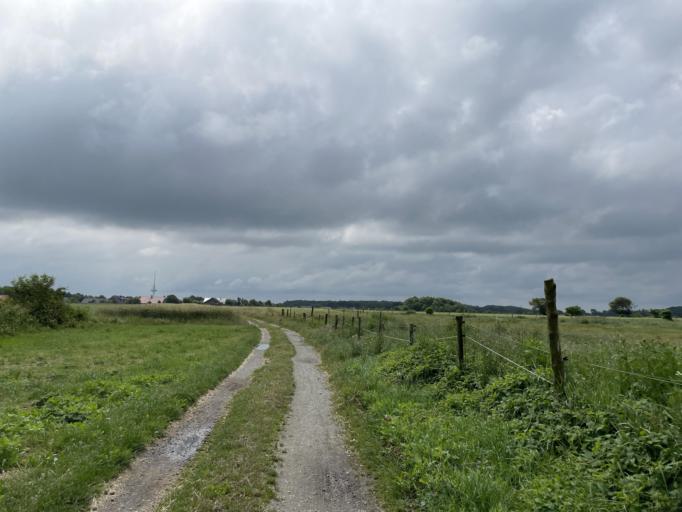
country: DE
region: Lower Saxony
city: Cuxhaven
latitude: 53.8782
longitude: 8.6450
